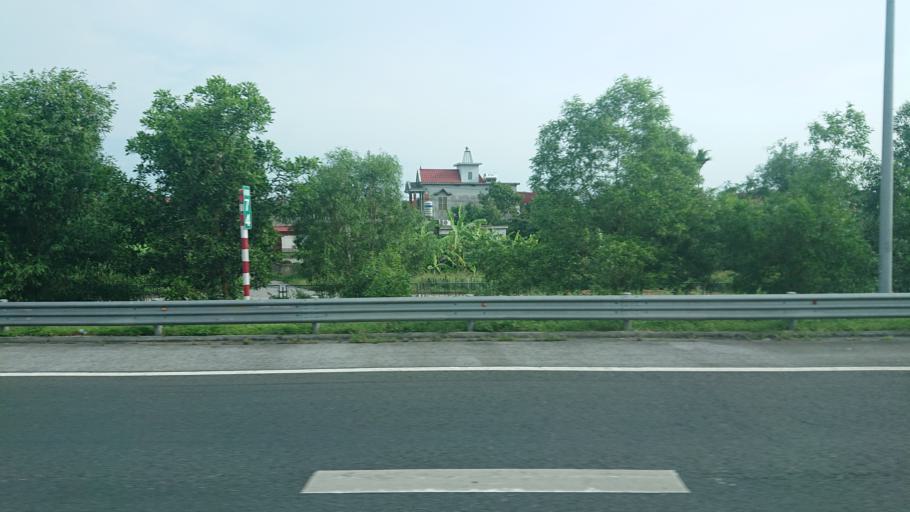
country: VN
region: Hai Phong
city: An Lao
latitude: 20.8040
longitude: 106.5228
